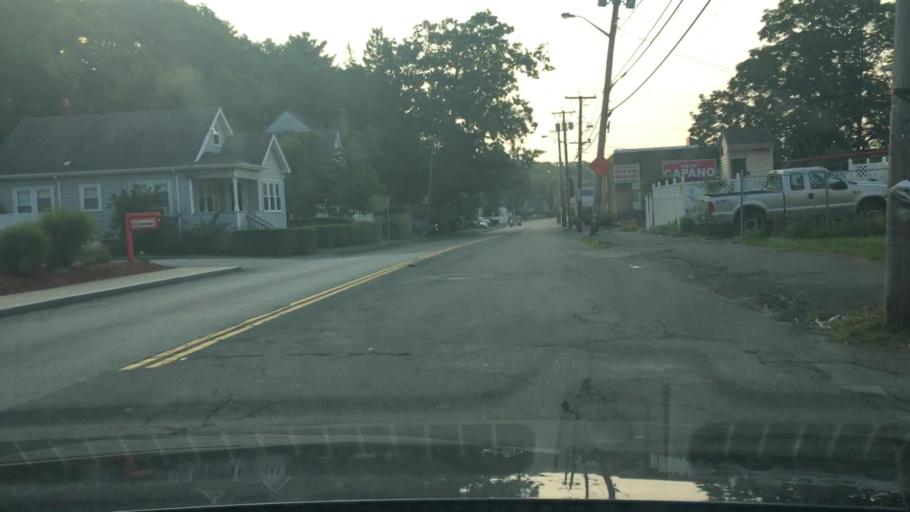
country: US
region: Massachusetts
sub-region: Essex County
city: Saugus
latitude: 42.4739
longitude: -70.9900
